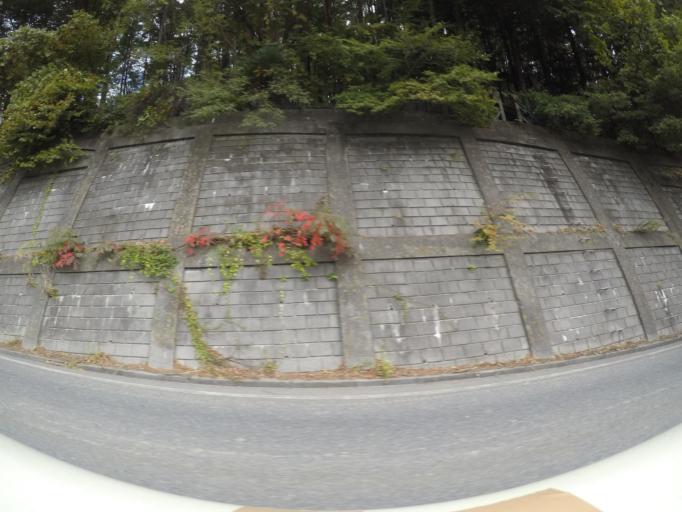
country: JP
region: Nagano
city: Chino
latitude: 35.9119
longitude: 138.0945
